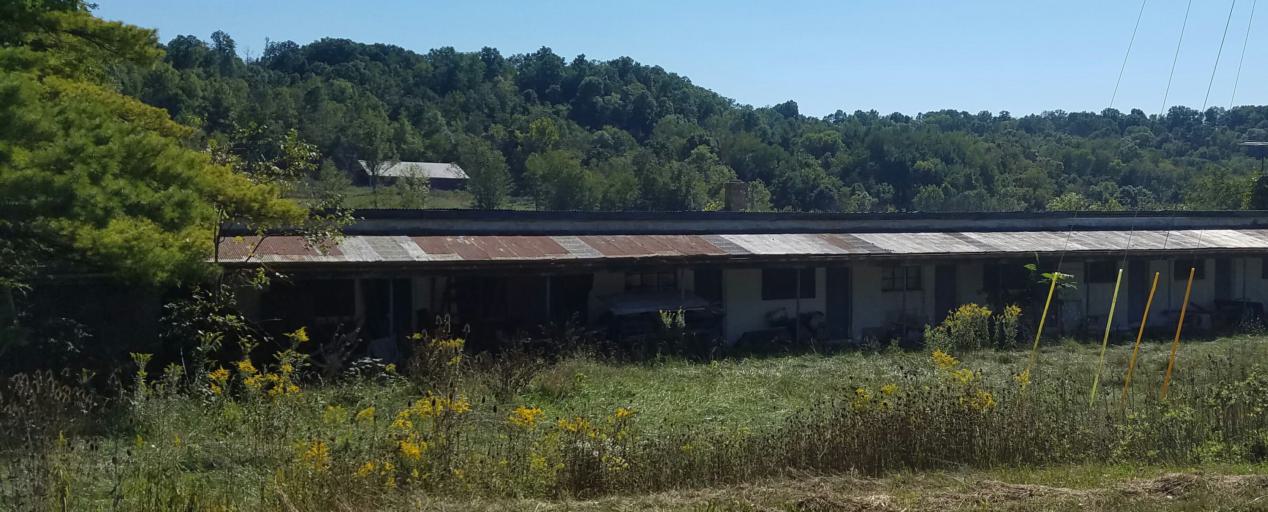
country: US
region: Ohio
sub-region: Belmont County
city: Barnesville
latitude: 40.0516
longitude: -81.3330
